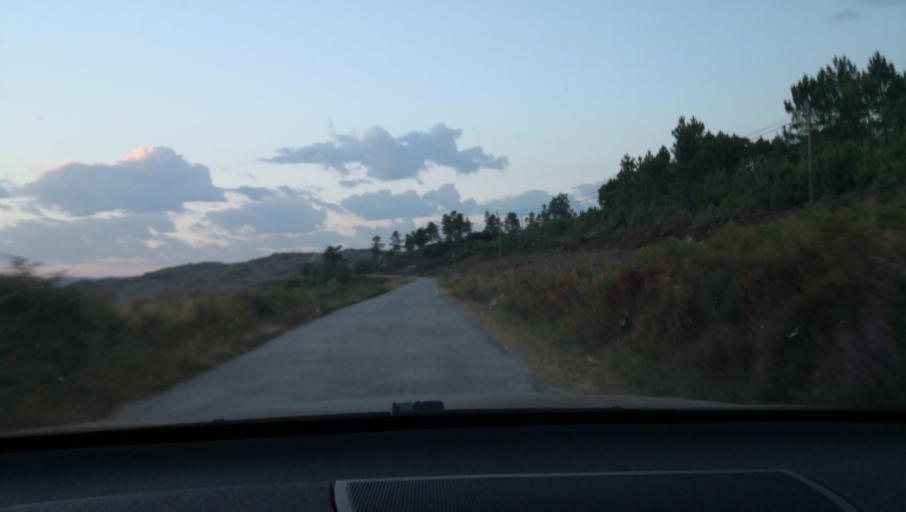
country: PT
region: Vila Real
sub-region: Sabrosa
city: Sabrosa
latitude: 41.2727
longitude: -7.6254
